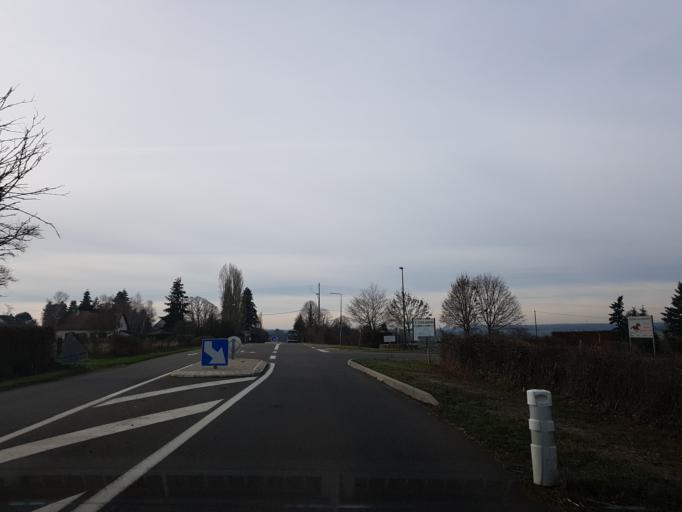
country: FR
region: Auvergne
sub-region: Departement de l'Allier
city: Neuvy
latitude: 46.5537
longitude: 3.2659
